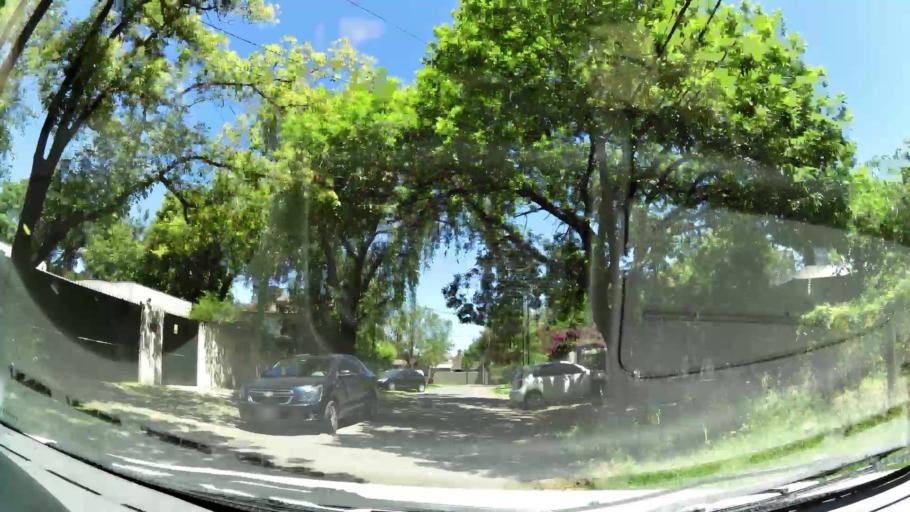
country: AR
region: Buenos Aires
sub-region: Partido de Tigre
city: Tigre
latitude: -34.4897
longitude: -58.5764
